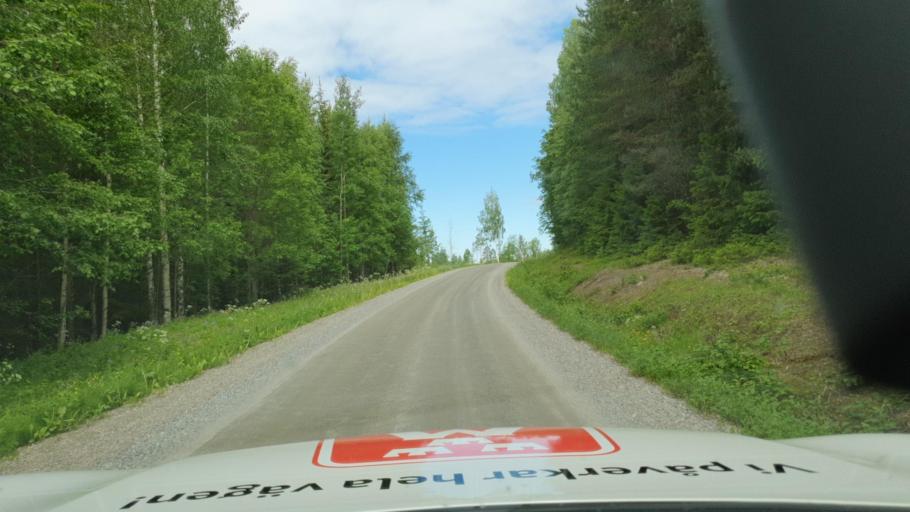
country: SE
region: Vaesterbotten
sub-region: Skelleftea Kommun
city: Forsbacka
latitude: 64.6443
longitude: 20.5398
